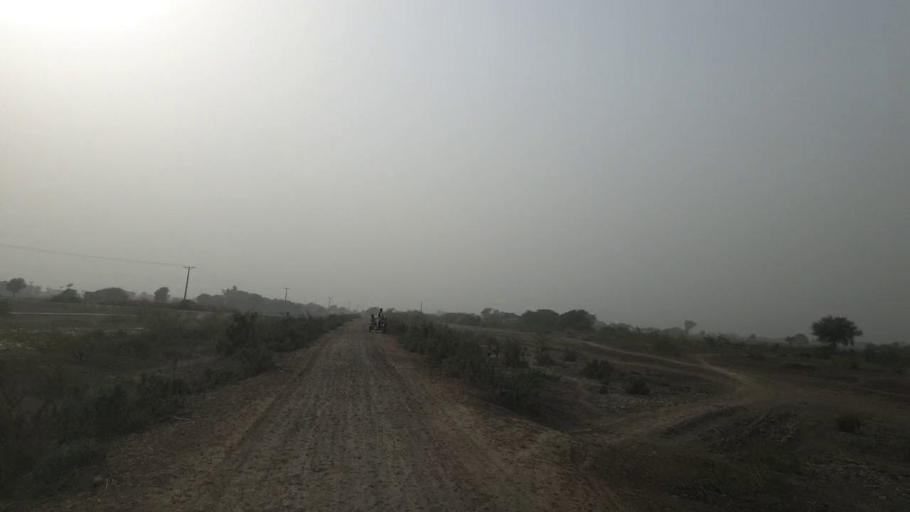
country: PK
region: Sindh
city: Kunri
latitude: 25.0669
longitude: 69.4723
